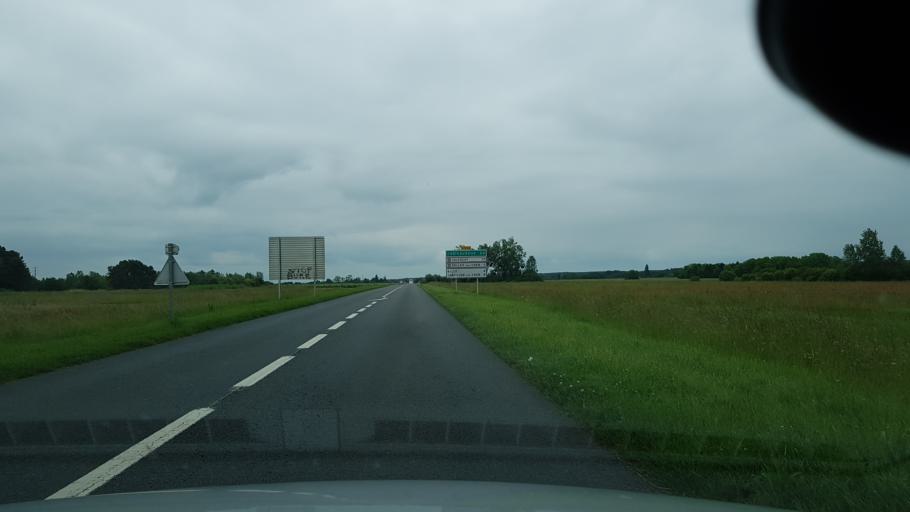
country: FR
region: Centre
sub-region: Departement du Loir-et-Cher
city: Chatillon-sur-Cher
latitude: 47.3198
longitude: 1.4970
